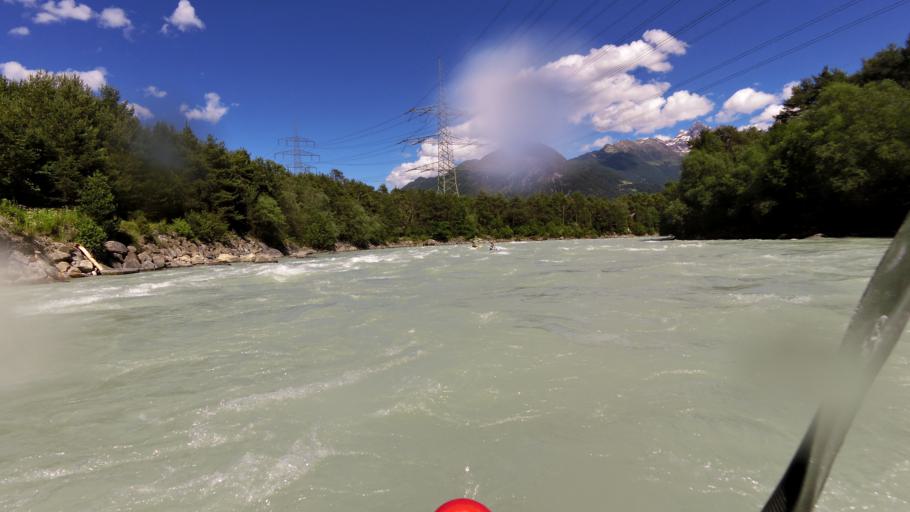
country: AT
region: Tyrol
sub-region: Politischer Bezirk Imst
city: Roppen
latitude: 47.2274
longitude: 10.8214
